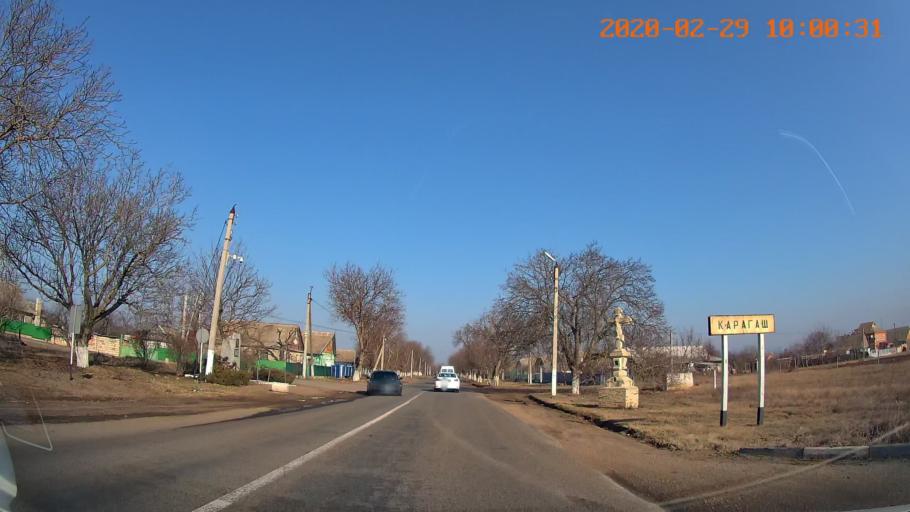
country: MD
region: Telenesti
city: Slobozia
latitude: 46.7689
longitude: 29.6862
